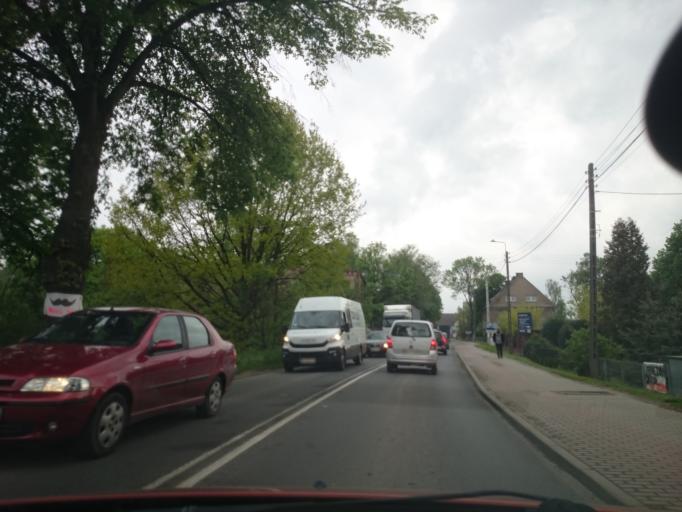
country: PL
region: Opole Voivodeship
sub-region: Powiat opolski
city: Czarnowasy
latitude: 50.7228
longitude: 17.9004
